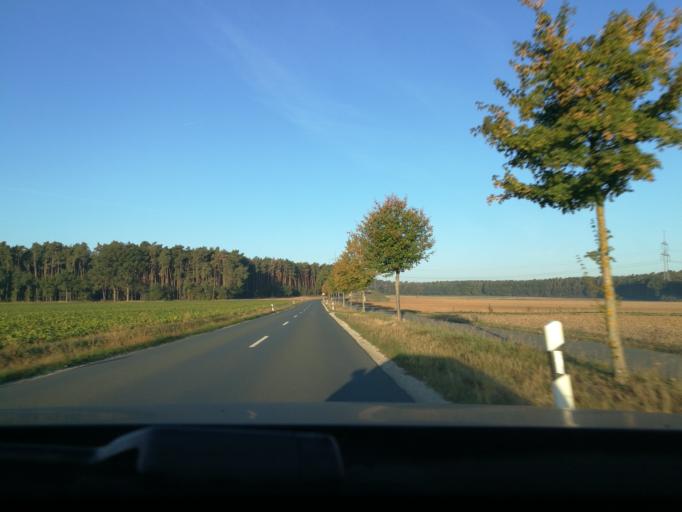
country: DE
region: Bavaria
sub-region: Regierungsbezirk Mittelfranken
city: Obermichelbach
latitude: 49.5289
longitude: 10.8951
